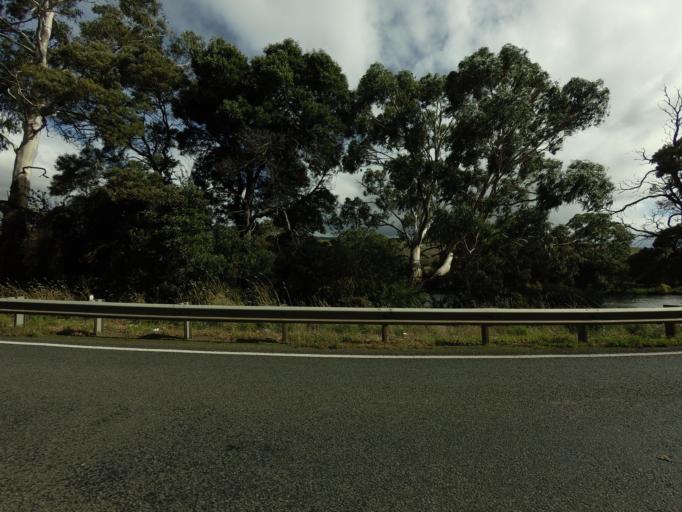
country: AU
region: Tasmania
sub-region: Derwent Valley
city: New Norfolk
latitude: -42.7269
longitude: 146.9550
